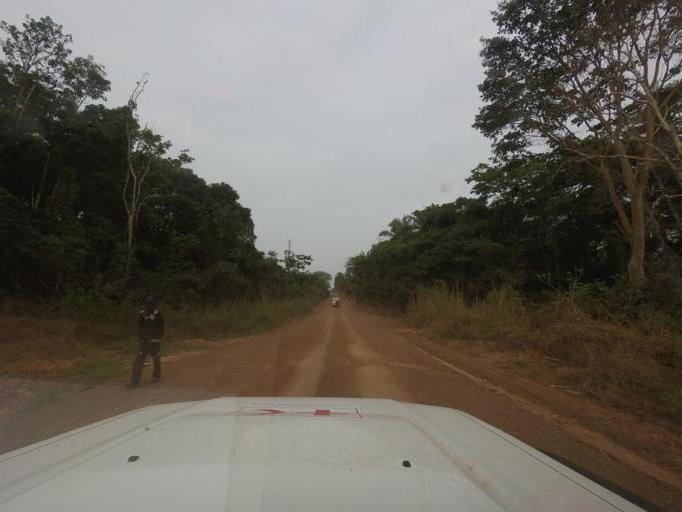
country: LR
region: Lofa
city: Voinjama
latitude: 8.3779
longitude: -9.8481
